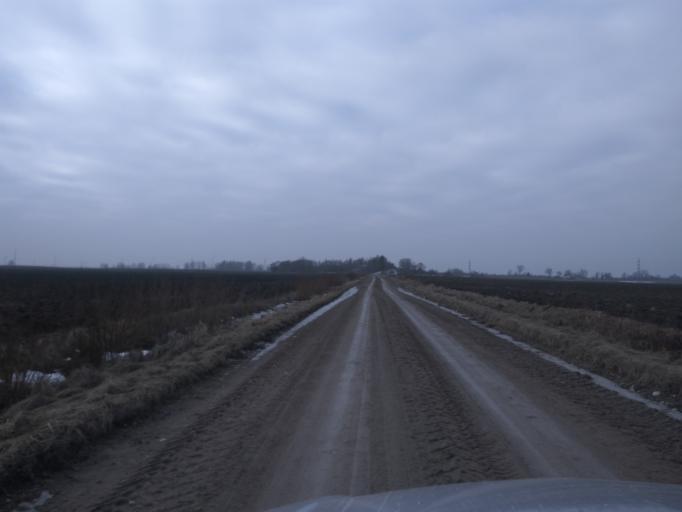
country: LV
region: Durbe
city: Liegi
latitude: 56.6697
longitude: 21.3717
